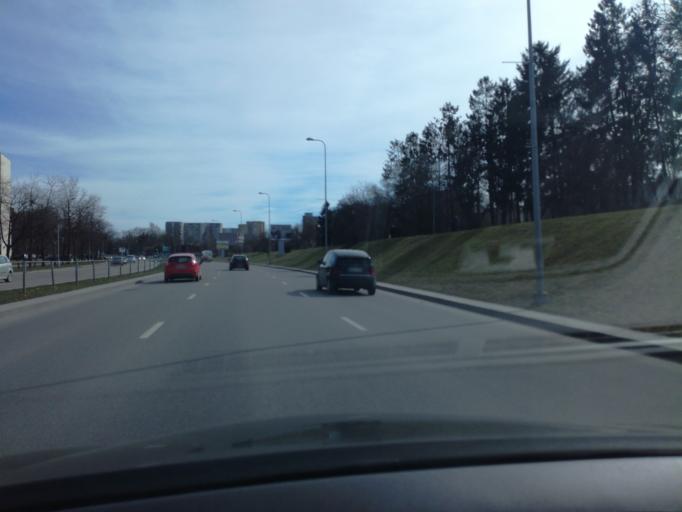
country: LT
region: Alytaus apskritis
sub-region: Alytus
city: Alytus
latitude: 54.3994
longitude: 24.0246
